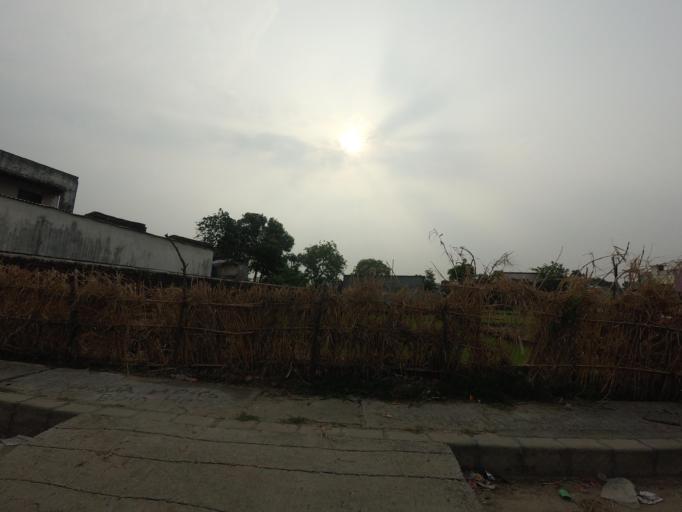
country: NP
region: Western Region
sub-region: Lumbini Zone
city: Bhairahawa
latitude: 27.4954
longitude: 83.4497
